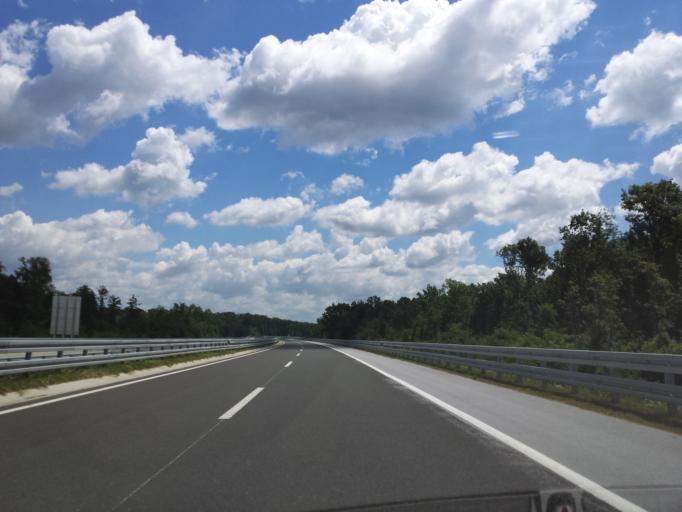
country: HR
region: Sisacko-Moslavacka
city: Lekenik
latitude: 45.5872
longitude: 16.1757
